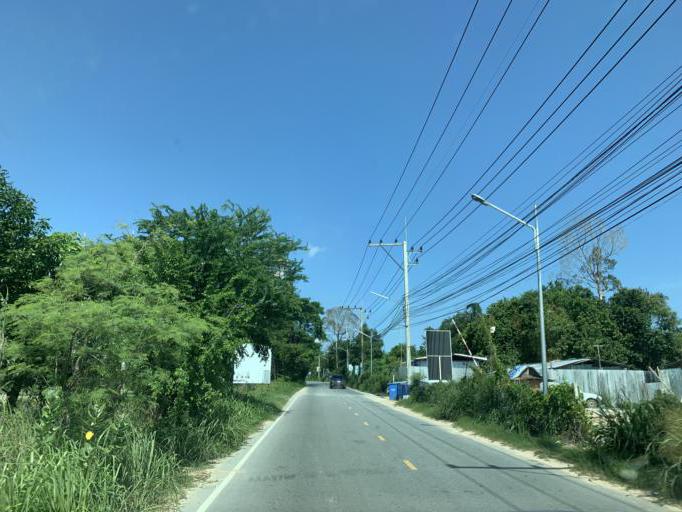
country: TH
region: Chon Buri
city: Sattahip
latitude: 12.7738
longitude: 100.9071
